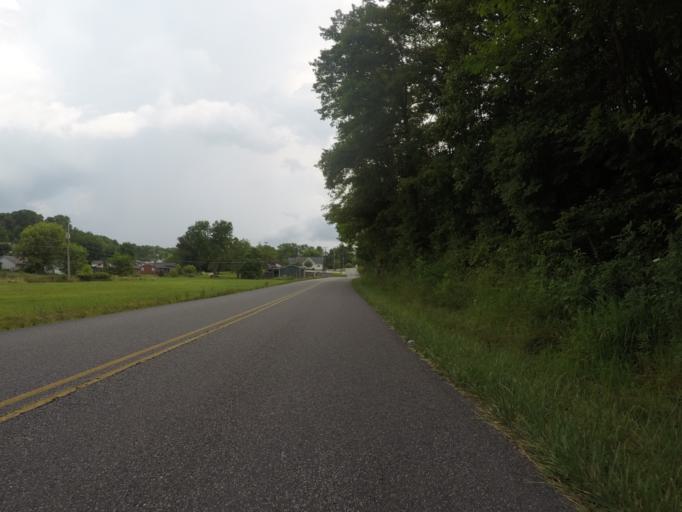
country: US
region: Kentucky
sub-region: Boyd County
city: Meads
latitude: 38.4299
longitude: -82.7080
